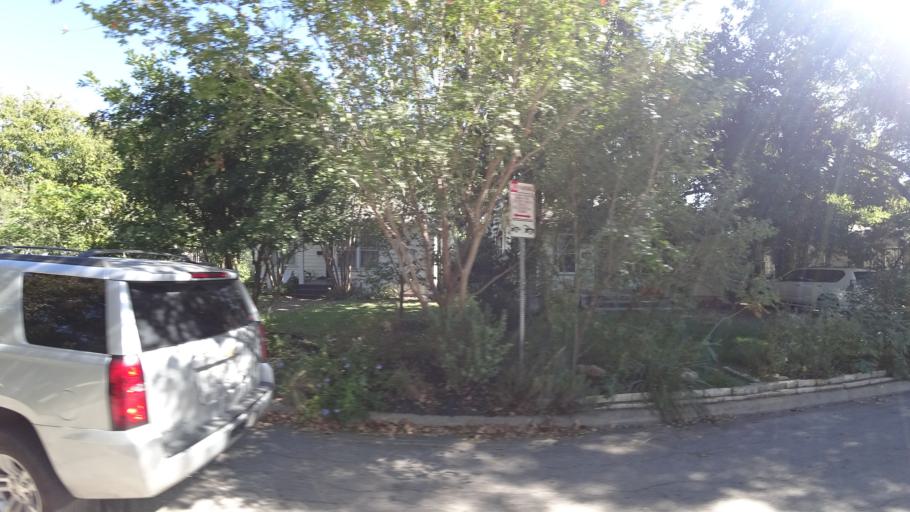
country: US
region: Texas
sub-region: Travis County
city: Austin
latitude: 30.3114
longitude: -97.7416
